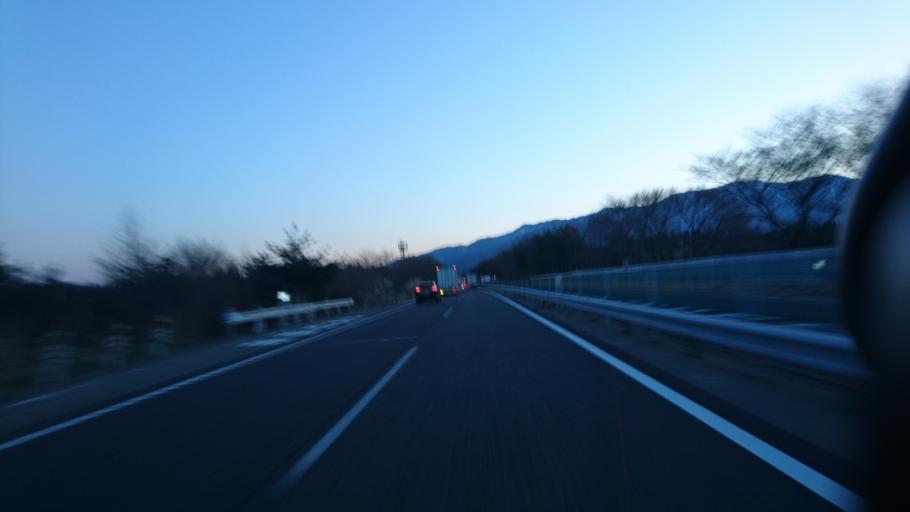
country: JP
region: Nagano
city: Ina
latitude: 35.8793
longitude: 137.9504
